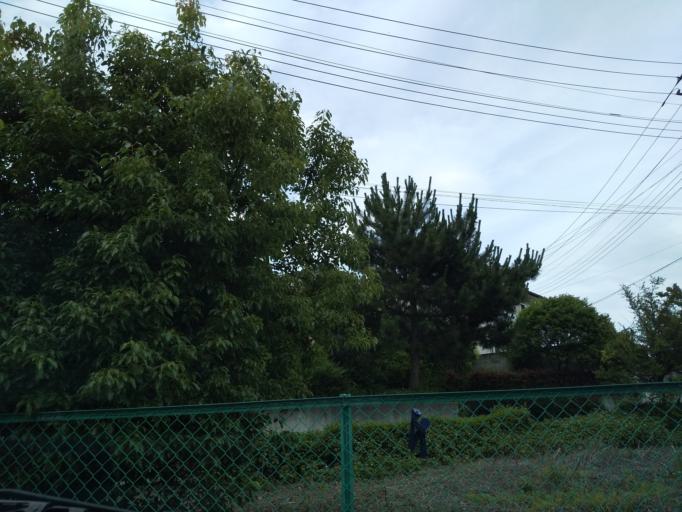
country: JP
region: Saitama
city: Kasukabe
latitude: 35.9940
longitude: 139.8119
